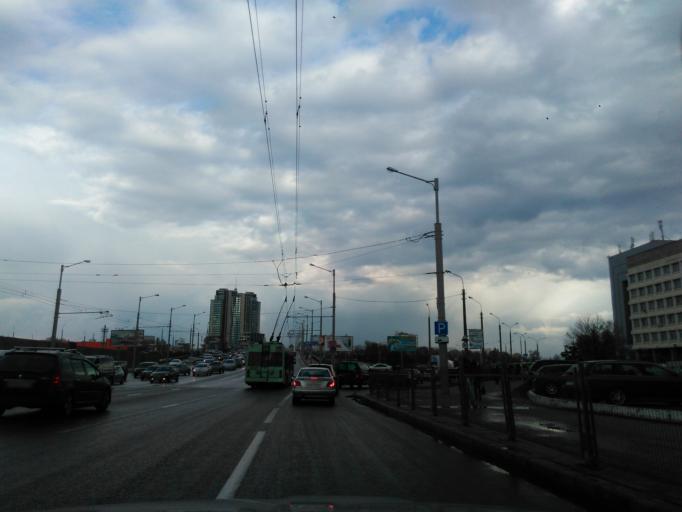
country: BY
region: Minsk
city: Minsk
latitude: 53.9073
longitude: 27.5192
